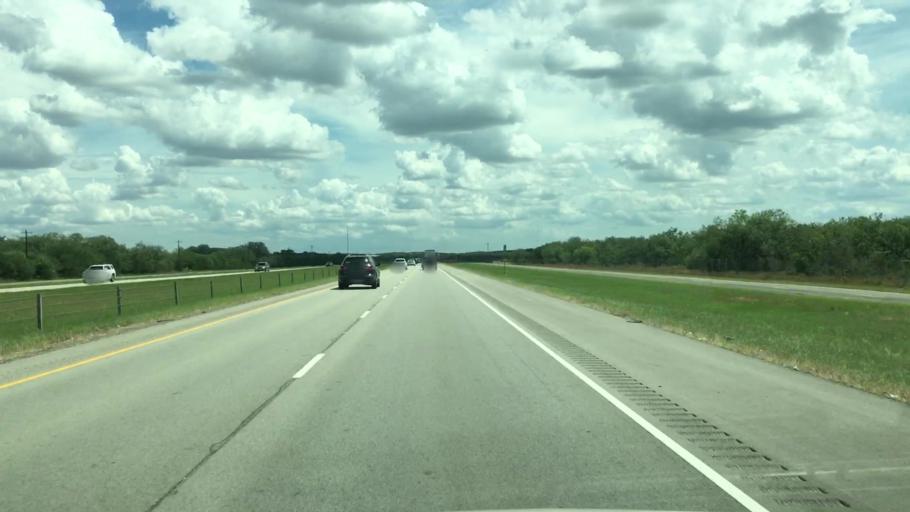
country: US
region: Texas
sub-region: Live Oak County
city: George West
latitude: 28.2747
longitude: -97.9487
